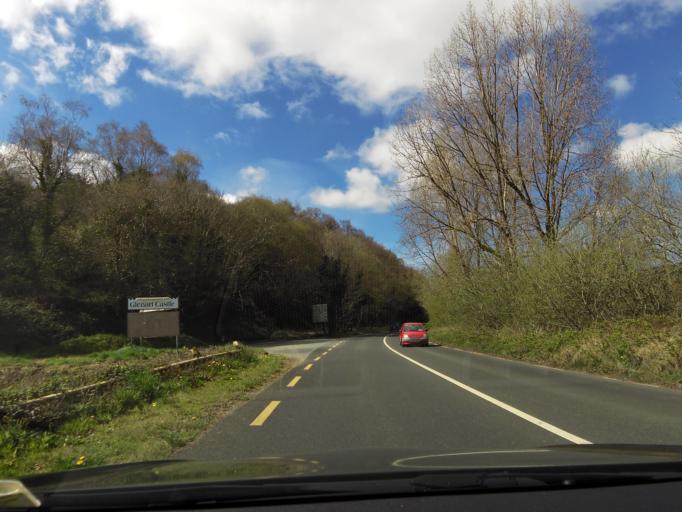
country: IE
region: Leinster
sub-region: Wicklow
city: Arklow
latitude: 52.8107
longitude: -6.1895
